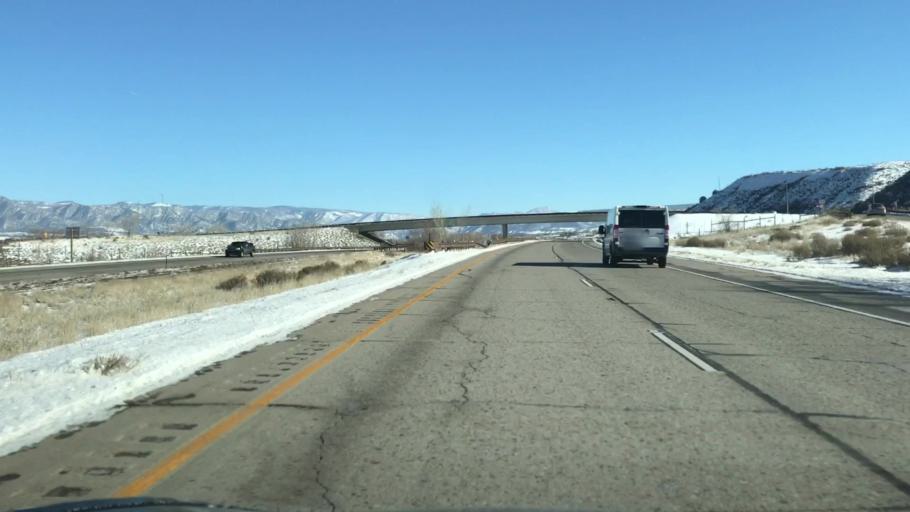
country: US
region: Colorado
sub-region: Garfield County
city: Silt
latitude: 39.5318
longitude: -107.7155
